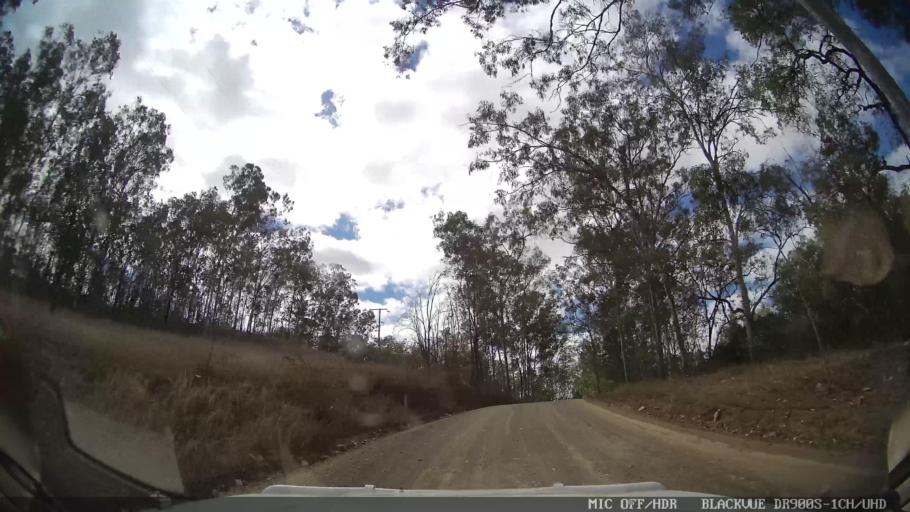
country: AU
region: Queensland
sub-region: Gladstone
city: Toolooa
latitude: -24.5526
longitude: 151.3365
